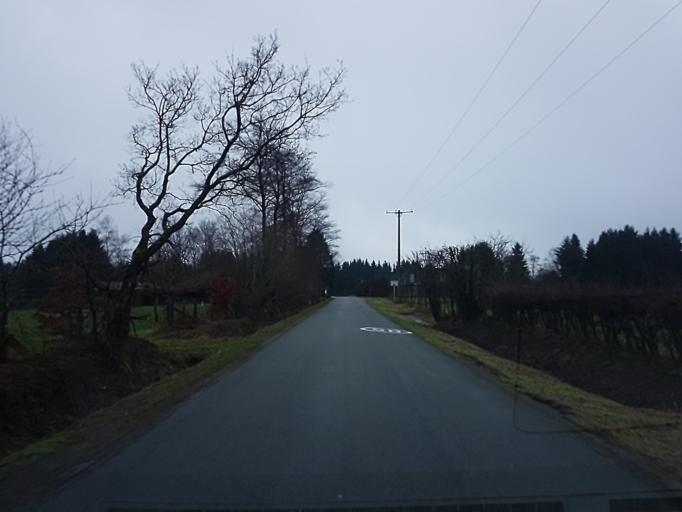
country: BE
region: Wallonia
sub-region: Province de Liege
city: Waimes
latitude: 50.4765
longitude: 6.1101
